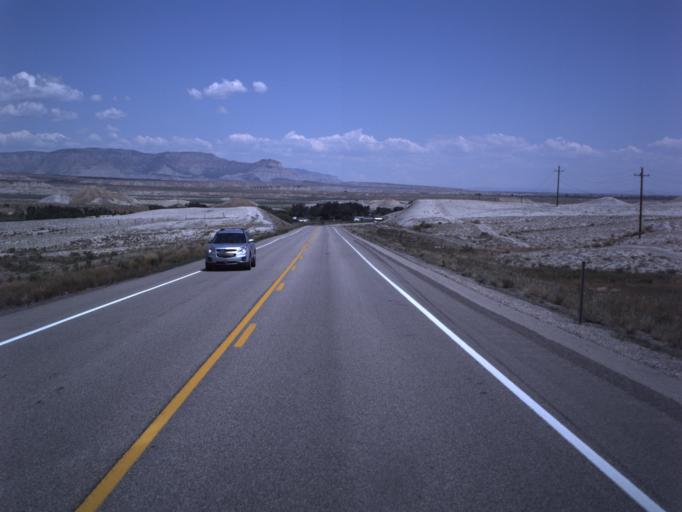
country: US
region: Utah
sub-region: Emery County
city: Ferron
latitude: 39.1402
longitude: -111.0966
